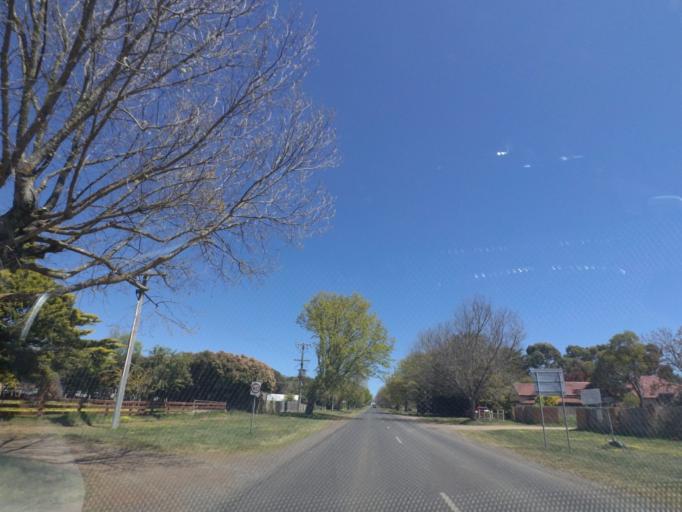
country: AU
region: Victoria
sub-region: Hume
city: Sunbury
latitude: -37.2791
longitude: 144.7302
